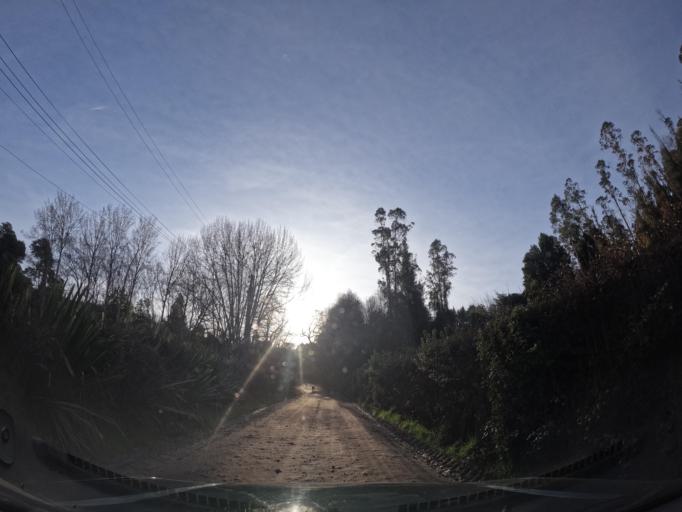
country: CL
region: Biobio
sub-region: Provincia de Concepcion
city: Concepcion
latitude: -36.8670
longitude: -72.9971
